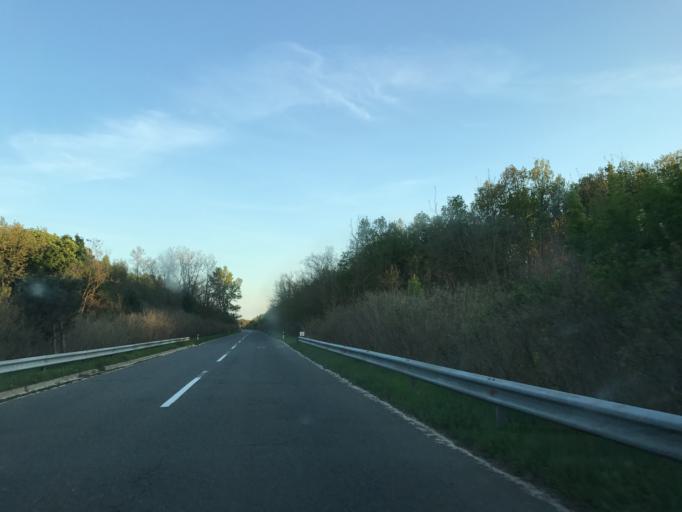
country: RO
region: Mehedinti
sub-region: Comuna Gogosu
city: Ostrovu Mare
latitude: 44.4505
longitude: 22.4534
